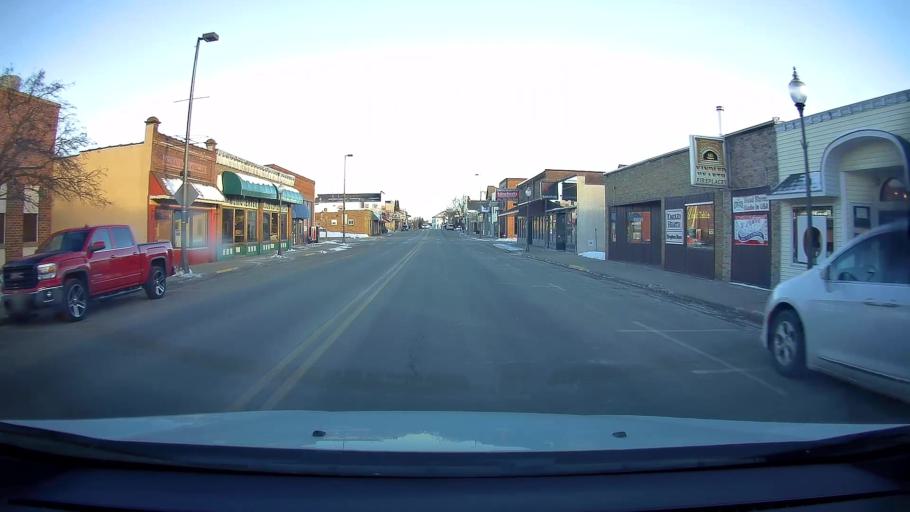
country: US
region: Wisconsin
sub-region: Barron County
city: Cumberland
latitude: 45.5333
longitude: -92.0215
